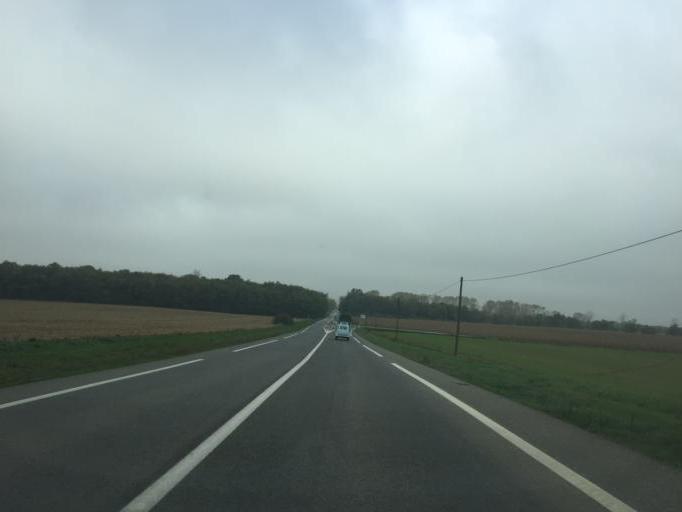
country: FR
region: Rhone-Alpes
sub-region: Departement de l'Ain
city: Villars-les-Dombes
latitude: 45.9654
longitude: 5.0057
